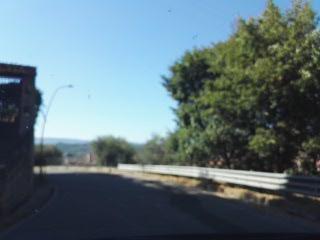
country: IT
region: Calabria
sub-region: Provincia di Vibo-Valentia
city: Sorianello
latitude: 38.5935
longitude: 16.2309
